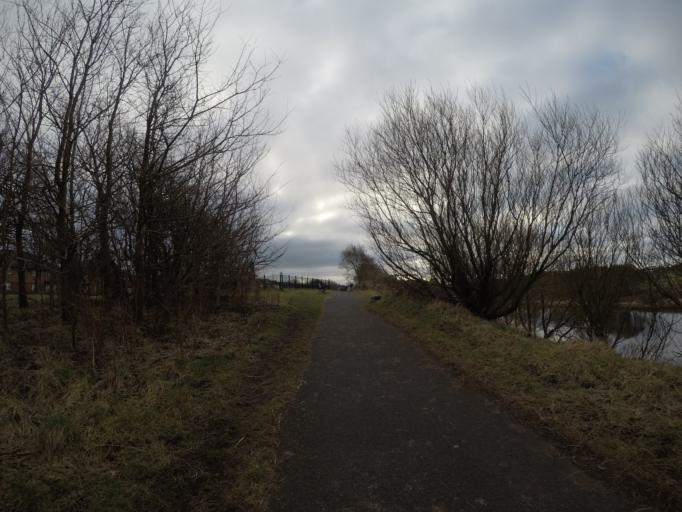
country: GB
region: Scotland
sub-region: North Ayrshire
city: Irvine
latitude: 55.6214
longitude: -4.6747
